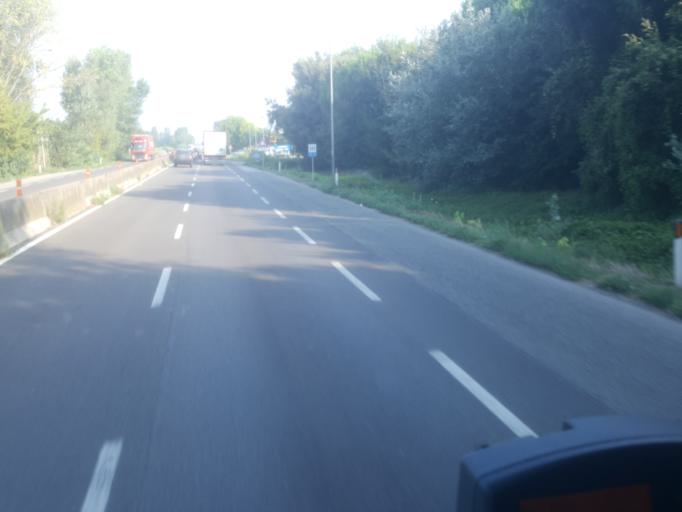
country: IT
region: Emilia-Romagna
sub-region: Provincia di Ravenna
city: Ravenna
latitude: 44.4008
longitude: 12.1797
